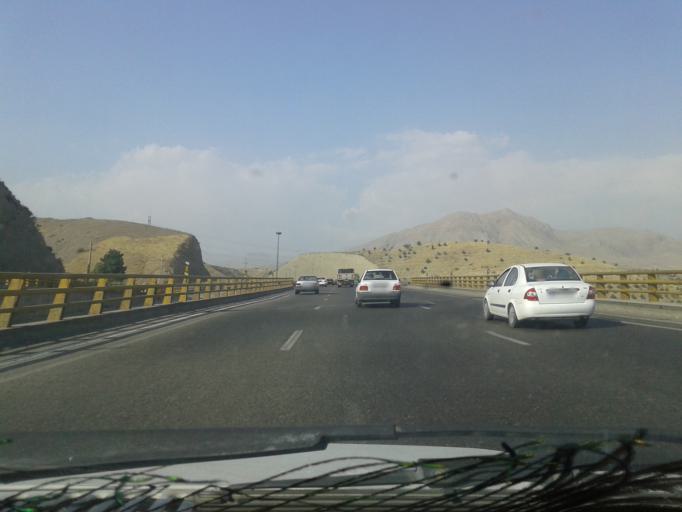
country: IR
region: Tehran
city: Pakdasht
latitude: 35.7342
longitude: 51.6787
